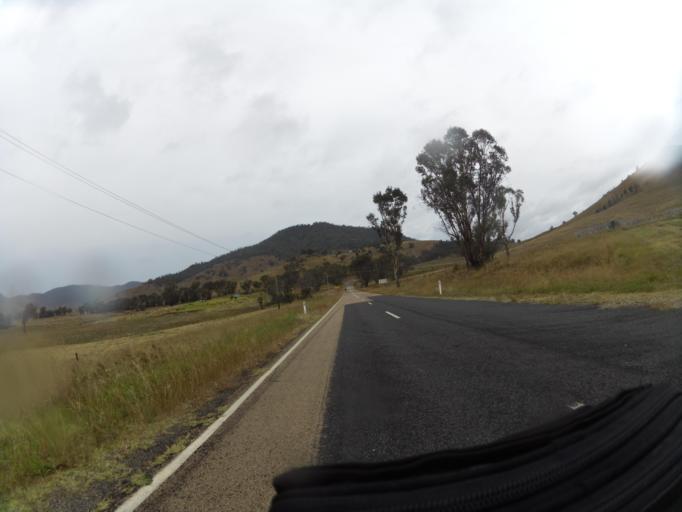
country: AU
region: New South Wales
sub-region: Greater Hume Shire
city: Holbrook
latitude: -36.2171
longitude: 147.7301
